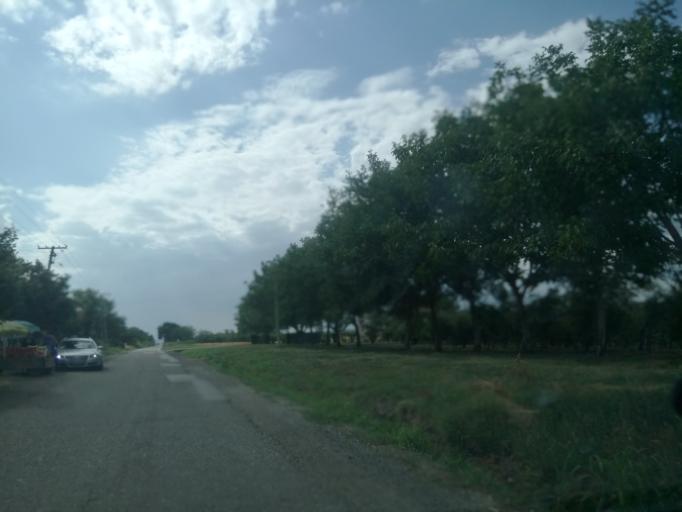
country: RS
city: Novi Slankamen
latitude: 45.1355
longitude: 20.2416
